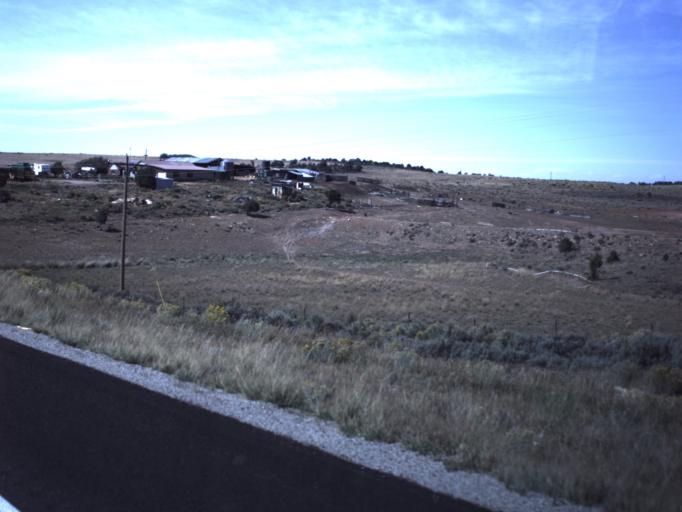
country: US
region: Utah
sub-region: San Juan County
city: Monticello
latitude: 37.8633
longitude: -109.2219
